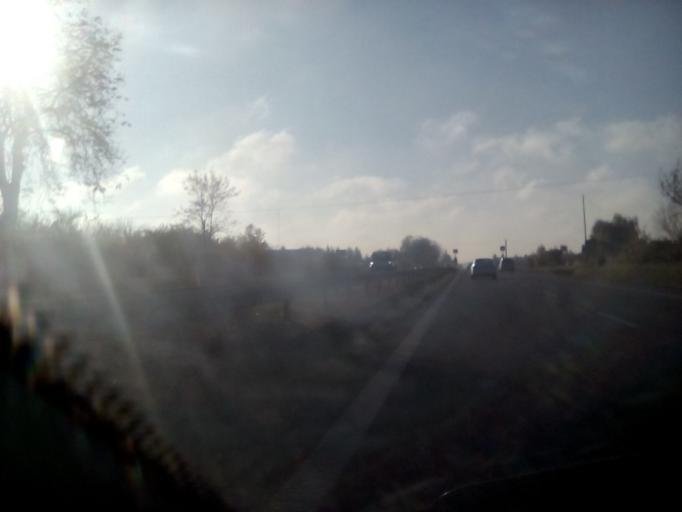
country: PL
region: Masovian Voivodeship
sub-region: Powiat piaseczynski
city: Tarczyn
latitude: 51.9367
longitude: 20.8471
